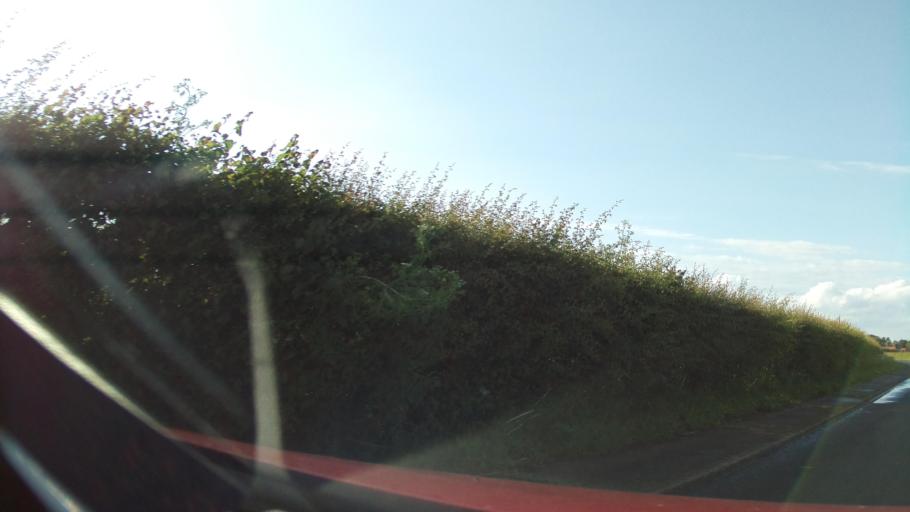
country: GB
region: England
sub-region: Lincolnshire
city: Navenby
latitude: 53.0654
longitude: -0.6363
